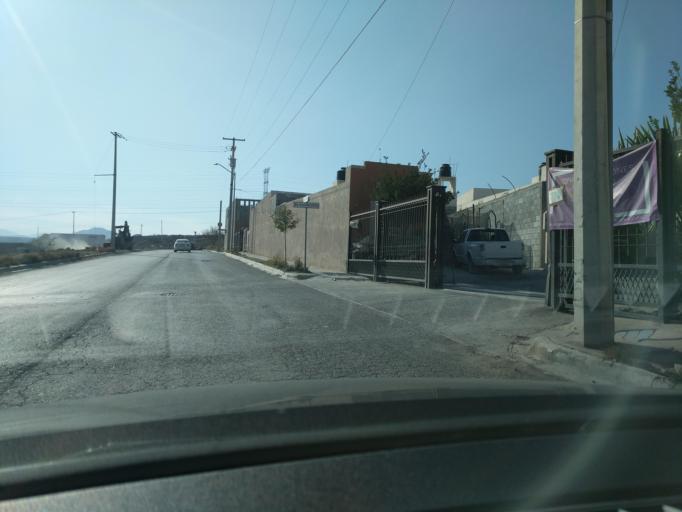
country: MX
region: Coahuila
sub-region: Ramos Arizpe
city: Ramos Arizpe
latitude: 25.5431
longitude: -100.9753
